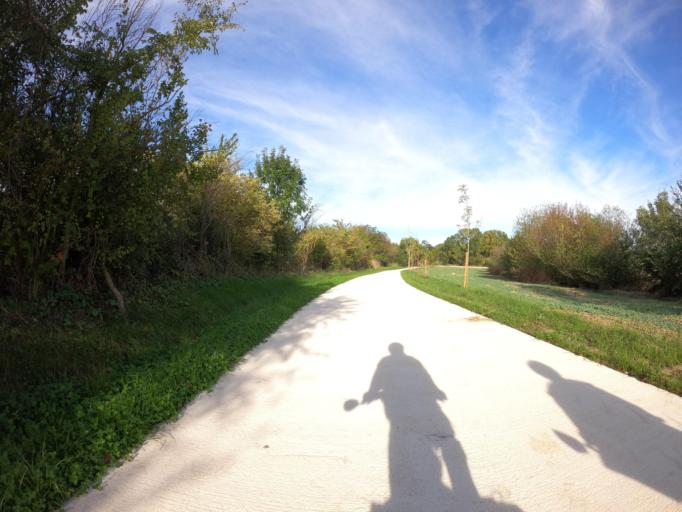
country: ES
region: Navarre
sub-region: Provincia de Navarra
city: Orkoien
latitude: 42.8119
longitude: -1.7371
